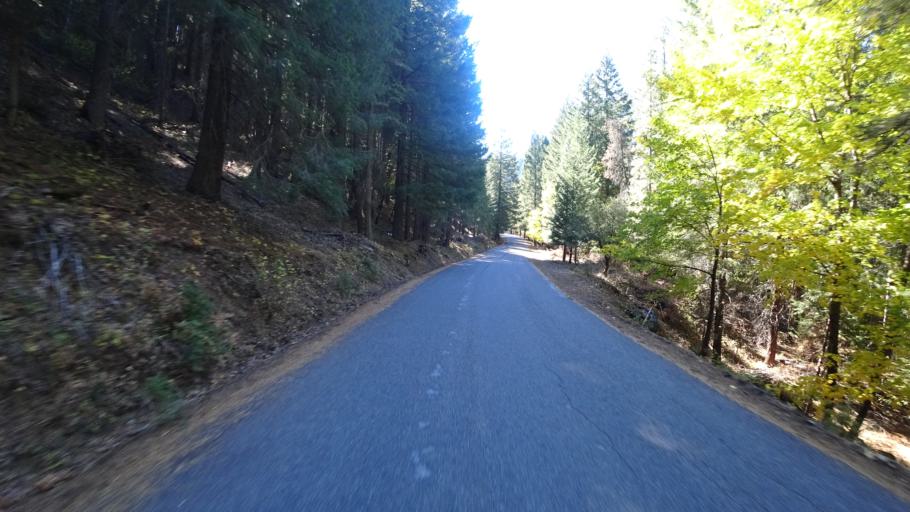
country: US
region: California
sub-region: Siskiyou County
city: Yreka
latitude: 41.3708
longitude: -123.0232
